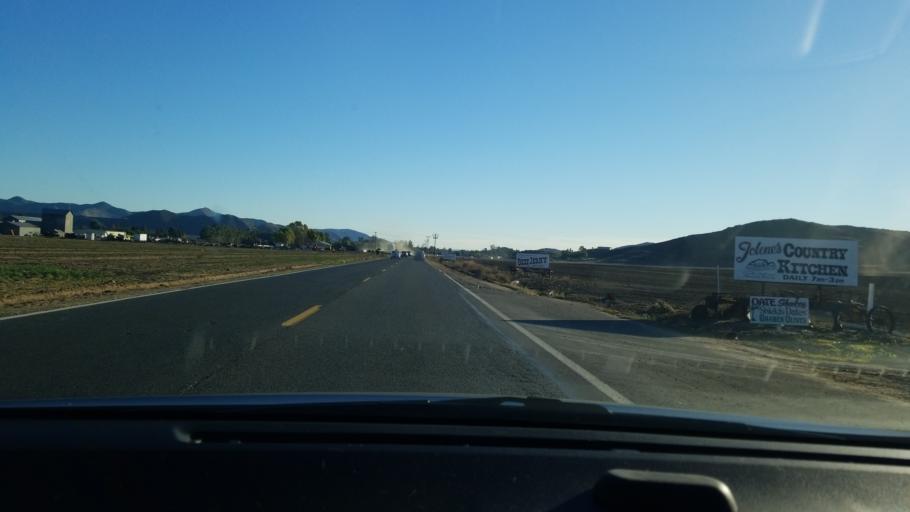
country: US
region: California
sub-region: Riverside County
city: Green Acres
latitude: 33.7266
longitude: -117.0764
